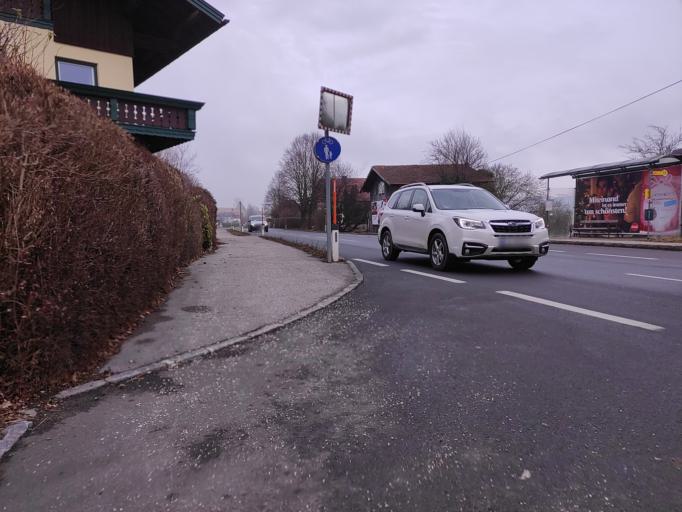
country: AT
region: Salzburg
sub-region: Politischer Bezirk Salzburg-Umgebung
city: Henndorf am Wallersee
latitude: 47.9160
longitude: 13.2039
